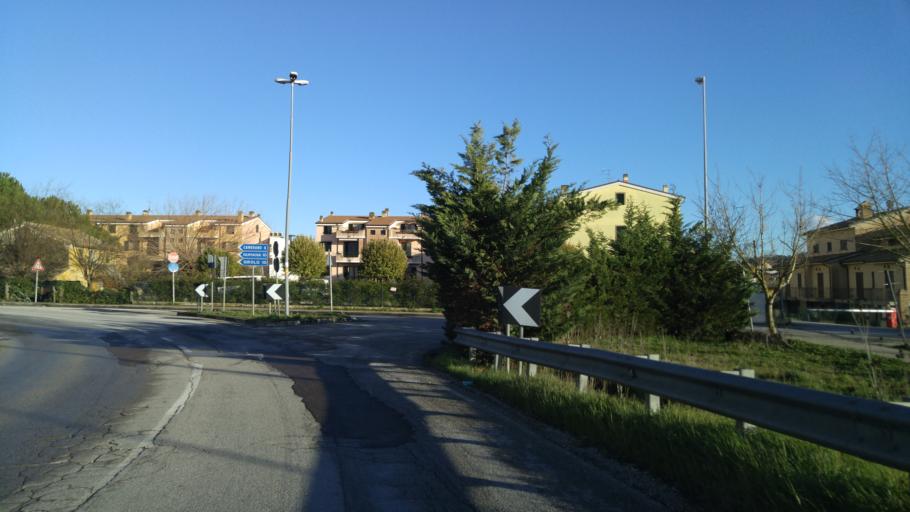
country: IT
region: The Marches
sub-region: Provincia di Ancona
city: Camerano
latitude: 43.4991
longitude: 13.5423
